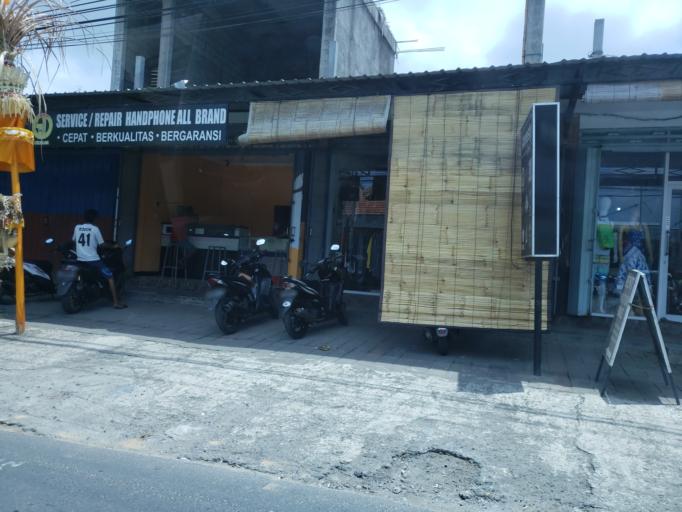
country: ID
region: Bali
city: Jimbaran
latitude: -8.8185
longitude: 115.1539
